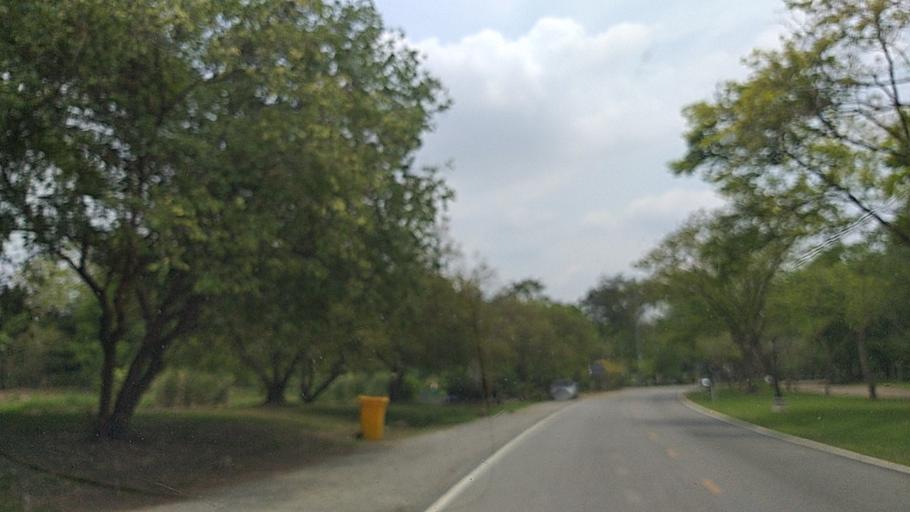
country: TH
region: Bangkok
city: Thawi Watthana
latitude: 13.7797
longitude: 100.3184
